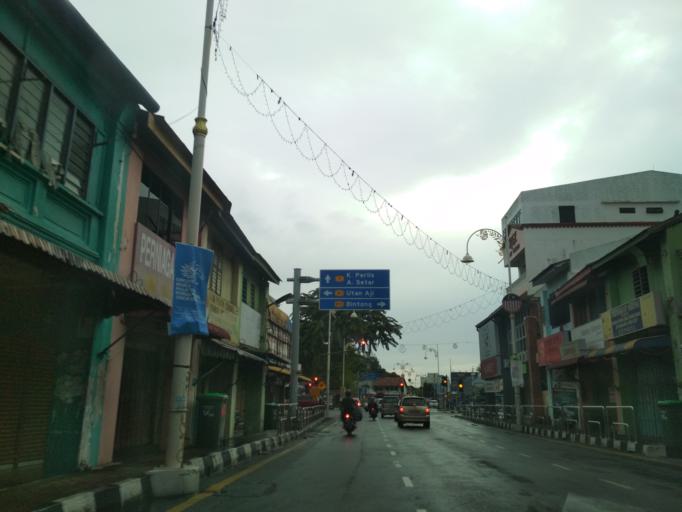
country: MY
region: Perlis
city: Kangar
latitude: 6.4381
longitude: 100.1947
